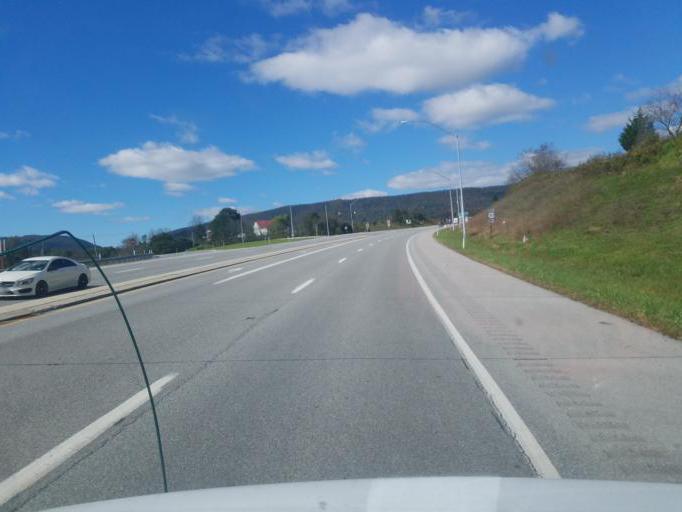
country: US
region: Pennsylvania
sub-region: Bedford County
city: Earlston
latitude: 40.0201
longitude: -78.3495
